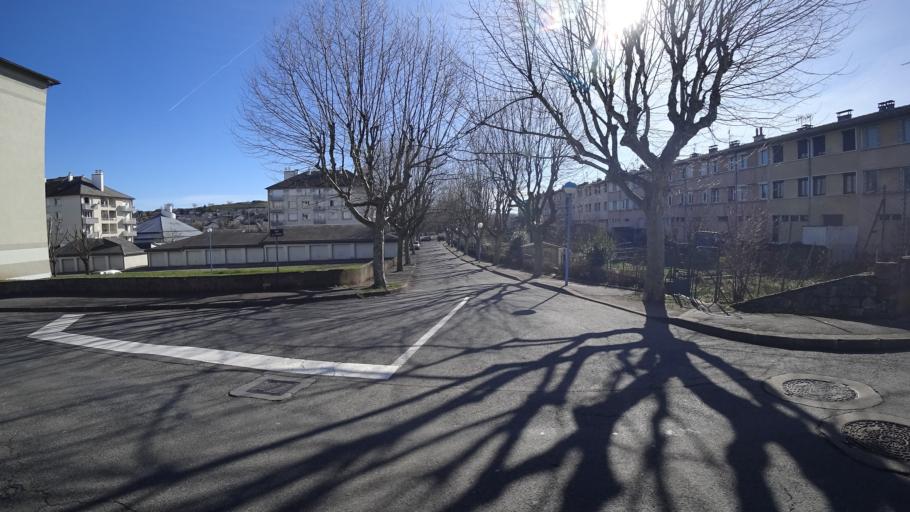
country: FR
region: Midi-Pyrenees
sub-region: Departement de l'Aveyron
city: Rodez
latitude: 44.3646
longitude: 2.5942
